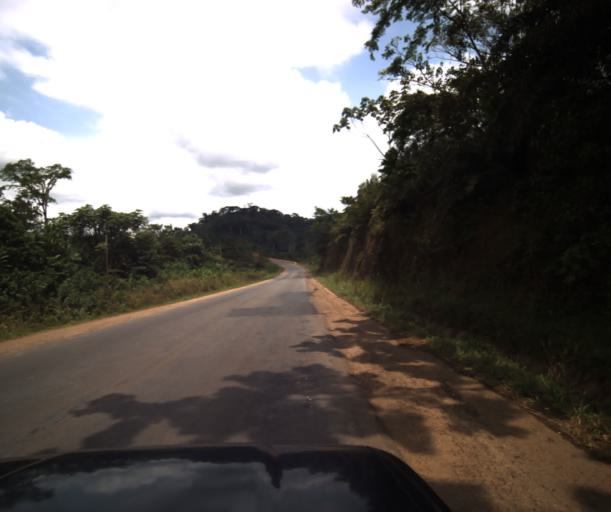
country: CM
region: Centre
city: Mbankomo
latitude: 3.7697
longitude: 11.0898
